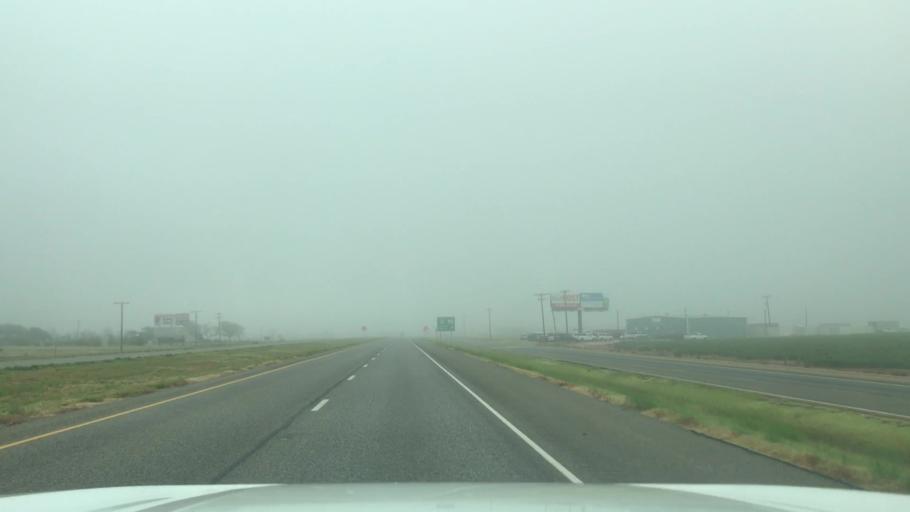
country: US
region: Texas
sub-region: Lubbock County
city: Slaton
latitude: 33.4252
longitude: -101.6521
